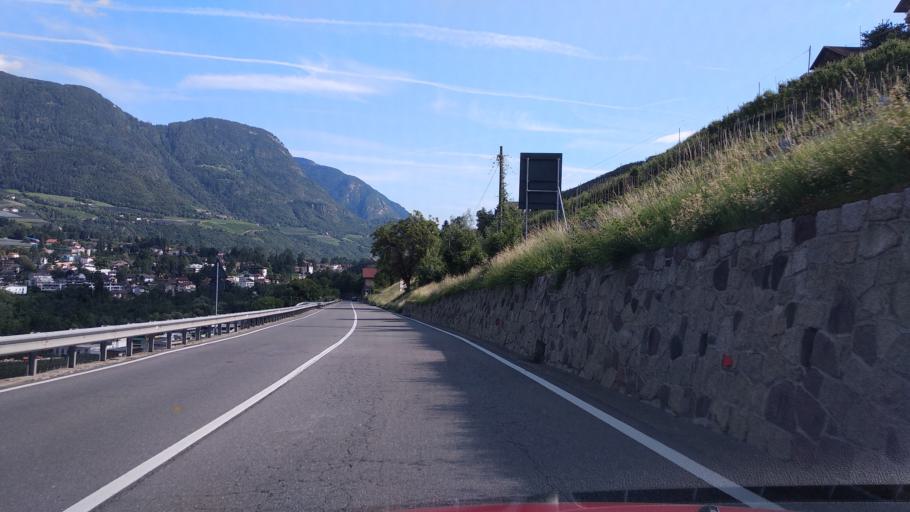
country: IT
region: Trentino-Alto Adige
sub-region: Bolzano
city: Merano
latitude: 46.6813
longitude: 11.1676
